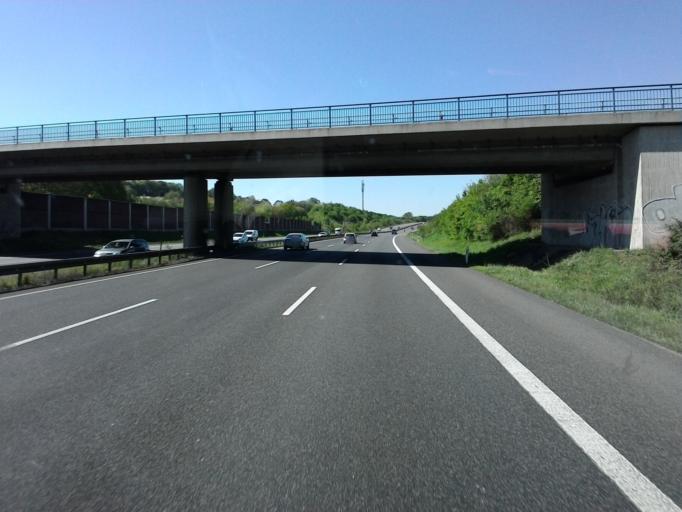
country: DE
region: North Rhine-Westphalia
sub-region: Regierungsbezirk Koln
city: Bad Honnef
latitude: 50.7060
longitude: 7.2505
